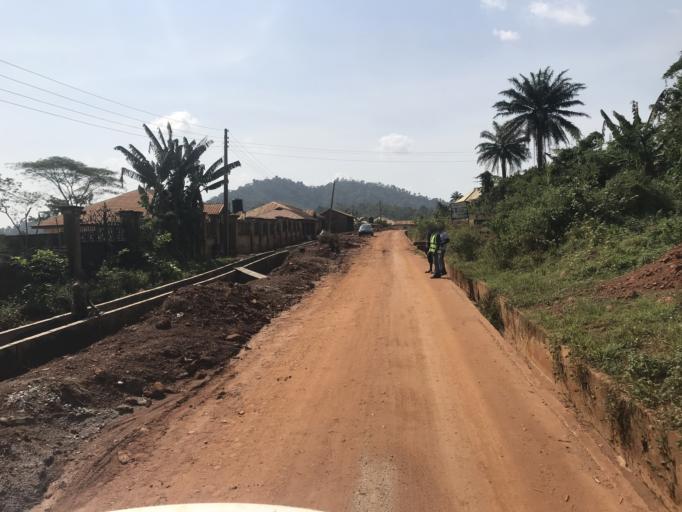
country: NG
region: Osun
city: Ilesa
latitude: 7.6213
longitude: 4.7018
